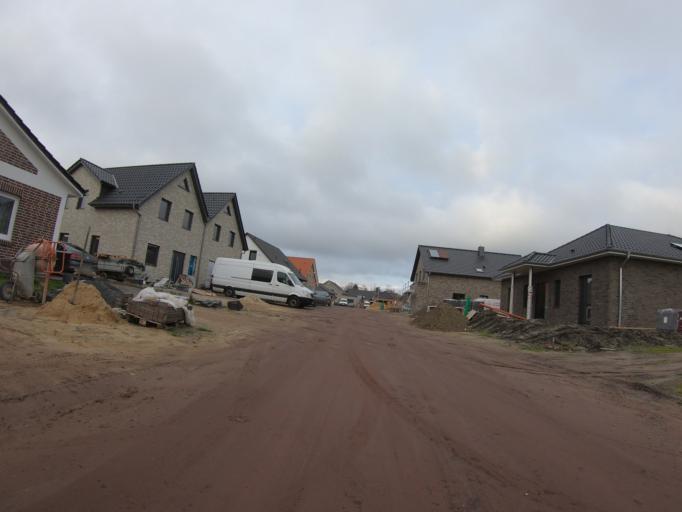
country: DE
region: Lower Saxony
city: Wesendorf
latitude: 52.5817
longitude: 10.5357
